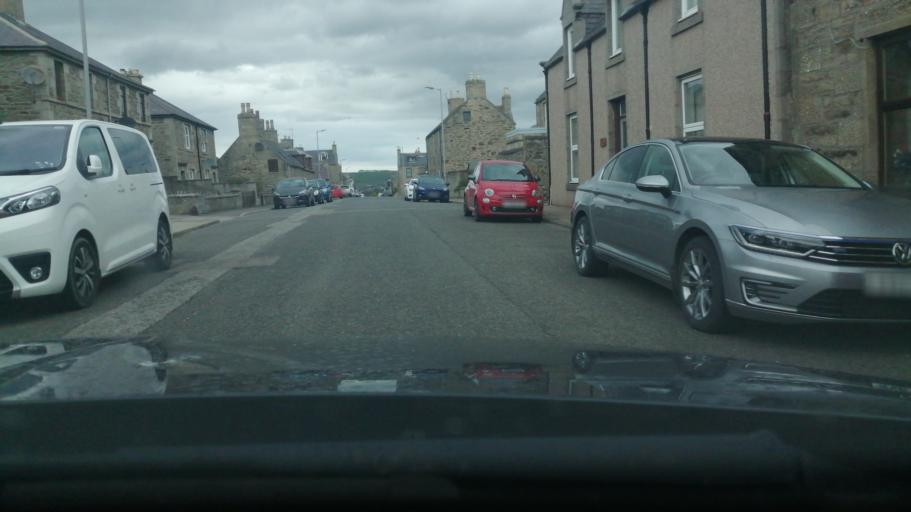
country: GB
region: Scotland
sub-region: Moray
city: Keith
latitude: 57.5373
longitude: -2.9527
